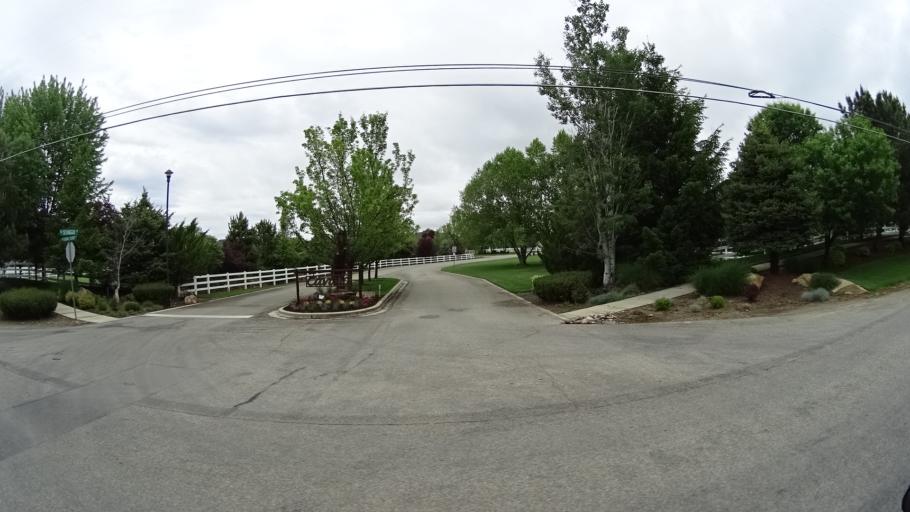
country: US
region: Idaho
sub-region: Ada County
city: Eagle
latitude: 43.7062
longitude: -116.3988
